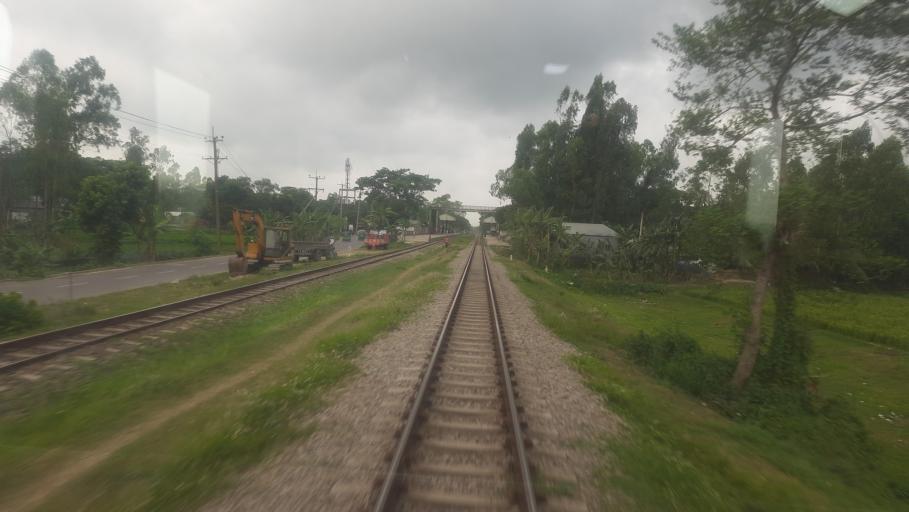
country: BD
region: Dhaka
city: Narsingdi
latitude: 23.9708
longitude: 90.8261
